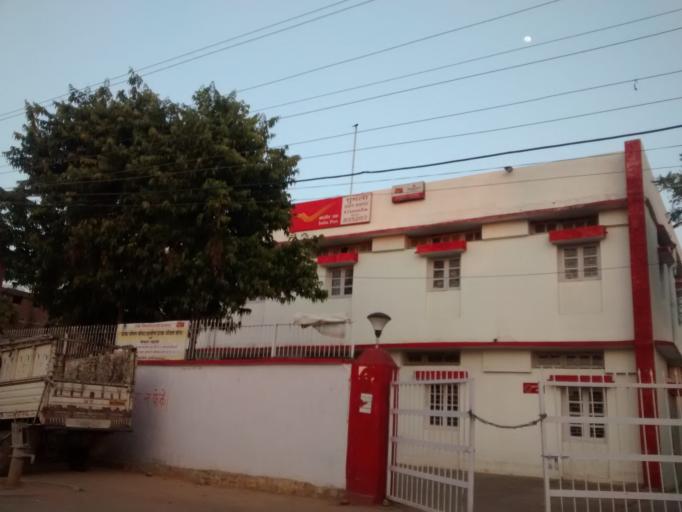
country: IN
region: Chhattisgarh
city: Gumla
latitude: 23.0438
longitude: 84.5411
